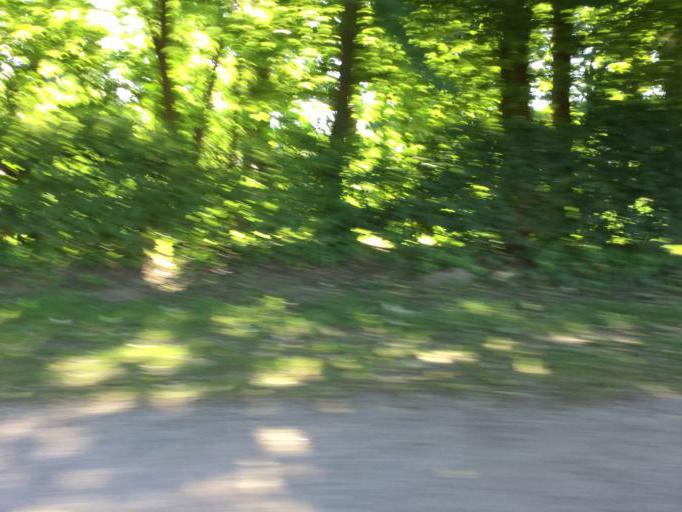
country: DE
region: Hamburg
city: Fuhlsbuettel
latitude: 53.6433
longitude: 10.0174
